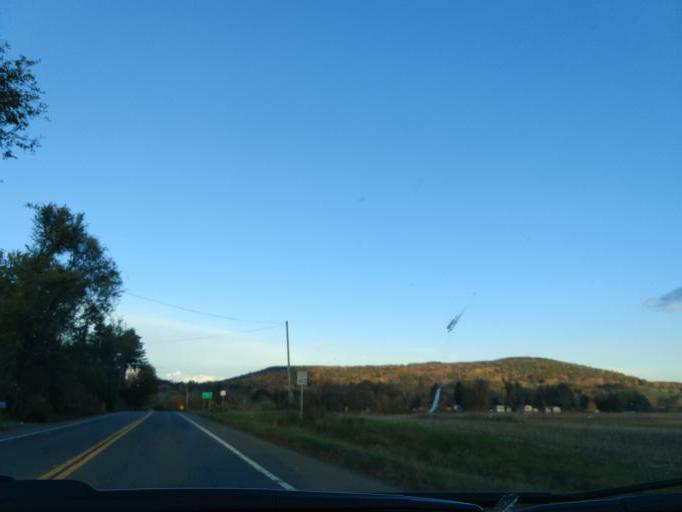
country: US
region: New York
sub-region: Tompkins County
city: Northeast Ithaca
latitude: 42.4513
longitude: -76.4488
